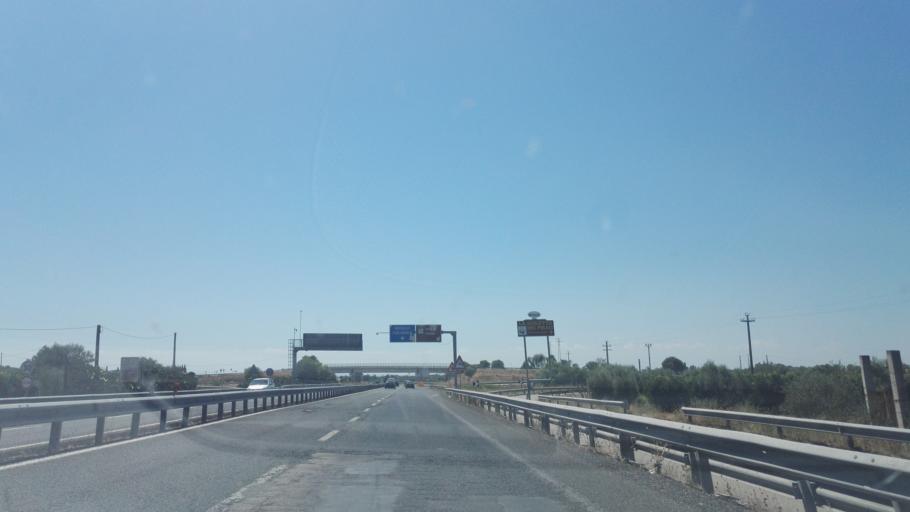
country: IT
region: Apulia
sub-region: Provincia di Taranto
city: Palagiano
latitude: 40.5232
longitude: 17.0303
